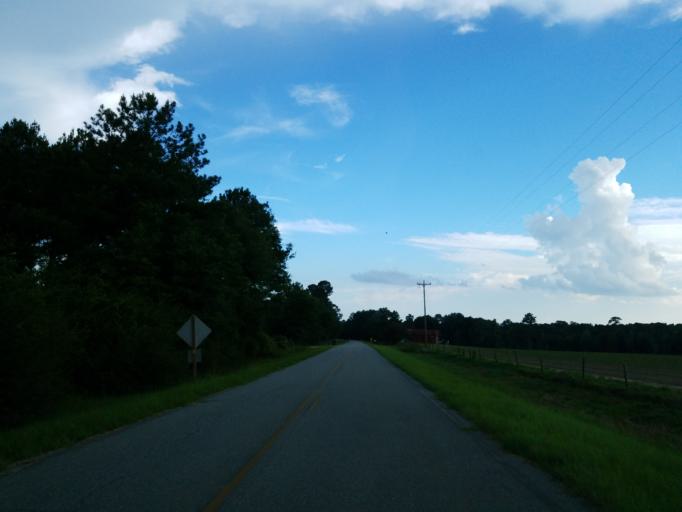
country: US
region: Georgia
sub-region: Tift County
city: Omega
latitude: 31.2620
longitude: -83.5140
